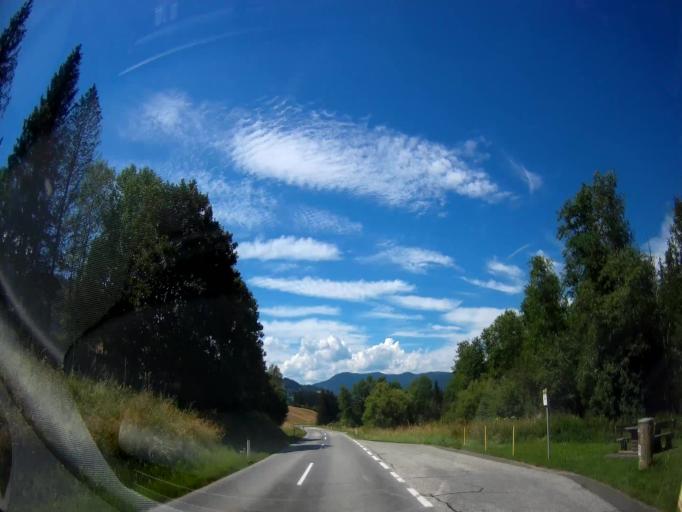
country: AT
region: Carinthia
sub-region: Politischer Bezirk Sankt Veit an der Glan
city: Glodnitz
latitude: 46.8579
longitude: 14.1320
